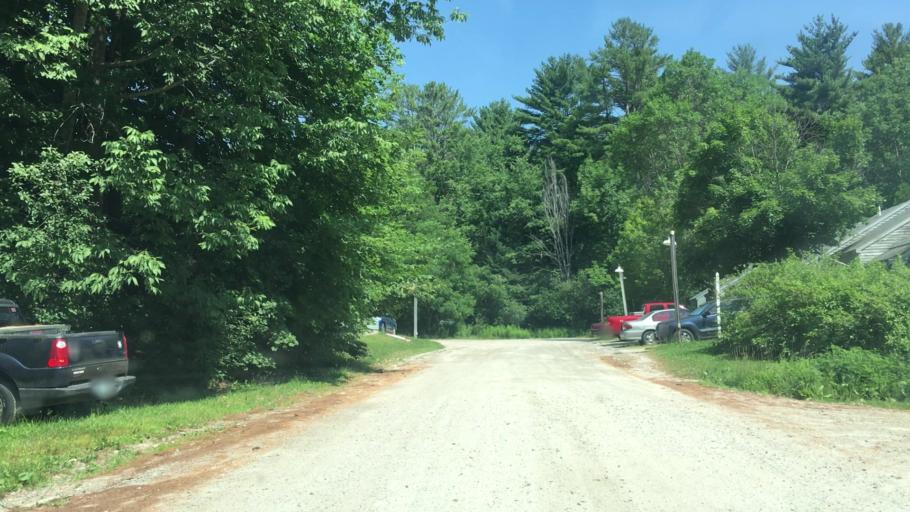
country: US
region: New Hampshire
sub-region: Sullivan County
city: Newport
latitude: 43.3709
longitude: -72.1647
